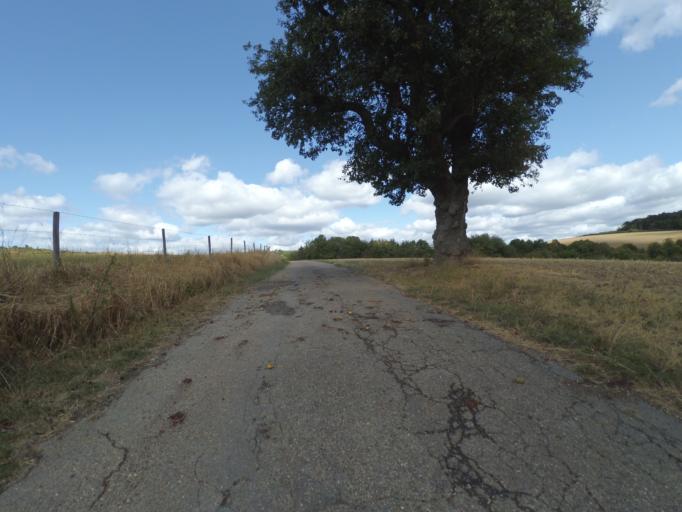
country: LU
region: Grevenmacher
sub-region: Canton de Remich
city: Lenningen
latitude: 49.6158
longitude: 6.3620
